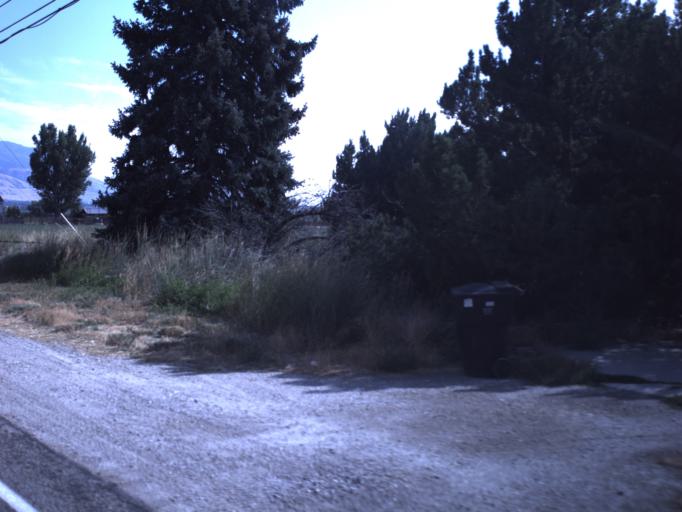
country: US
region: Utah
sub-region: Box Elder County
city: Honeyville
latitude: 41.5841
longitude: -112.0385
